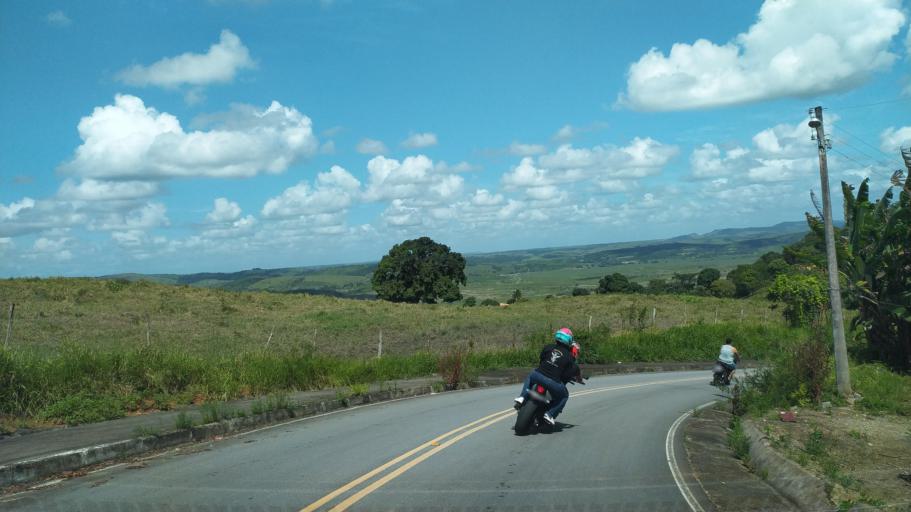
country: BR
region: Alagoas
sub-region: Uniao Dos Palmares
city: Uniao dos Palmares
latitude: -9.1629
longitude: -36.0677
